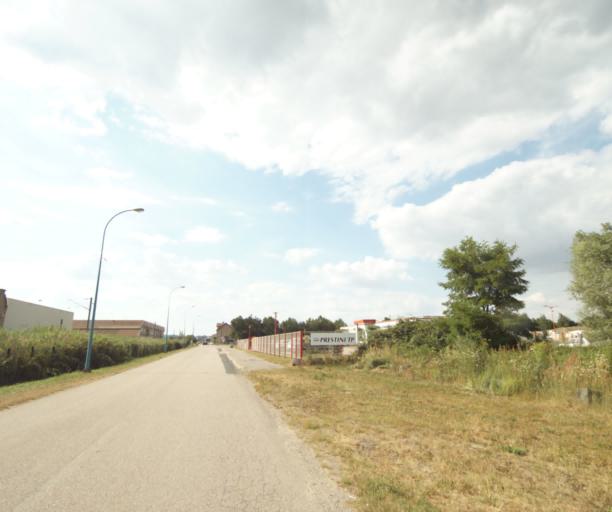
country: FR
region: Lorraine
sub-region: Departement de Meurthe-et-Moselle
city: Chanteheux
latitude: 48.5834
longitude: 6.5183
